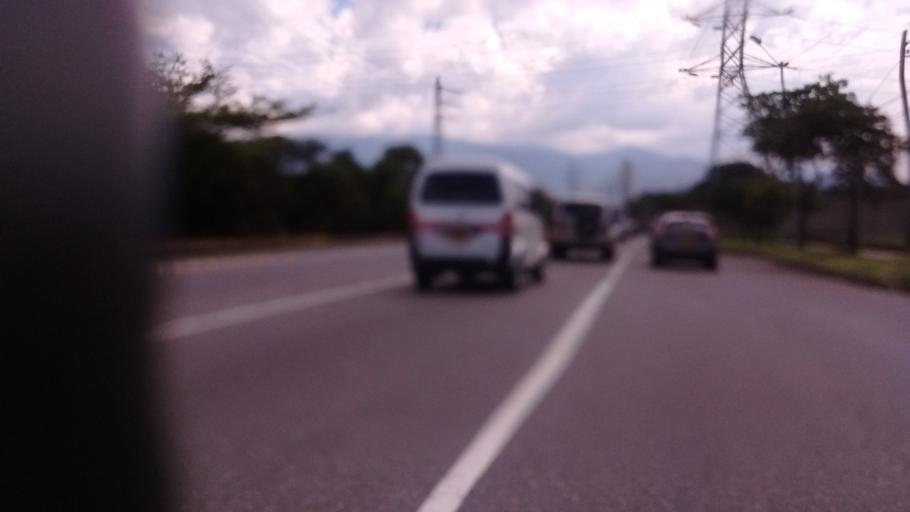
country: CO
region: Antioquia
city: Itagui
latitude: 6.2091
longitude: -75.5791
